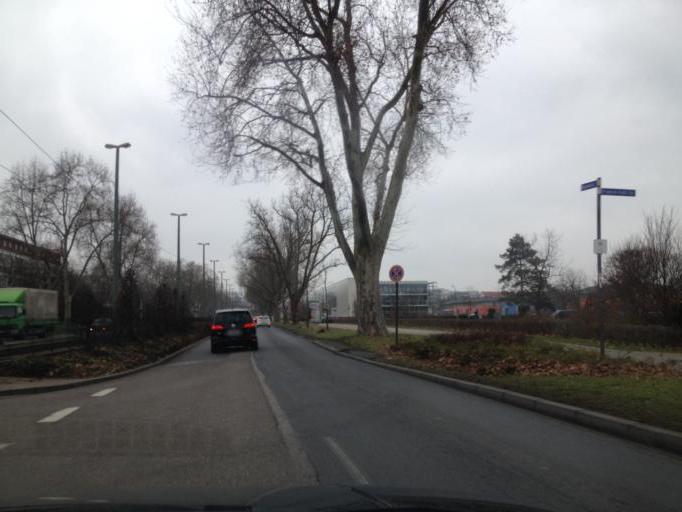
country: DE
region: Rheinland-Pfalz
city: Ludwigshafen am Rhein
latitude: 49.5026
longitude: 8.4163
